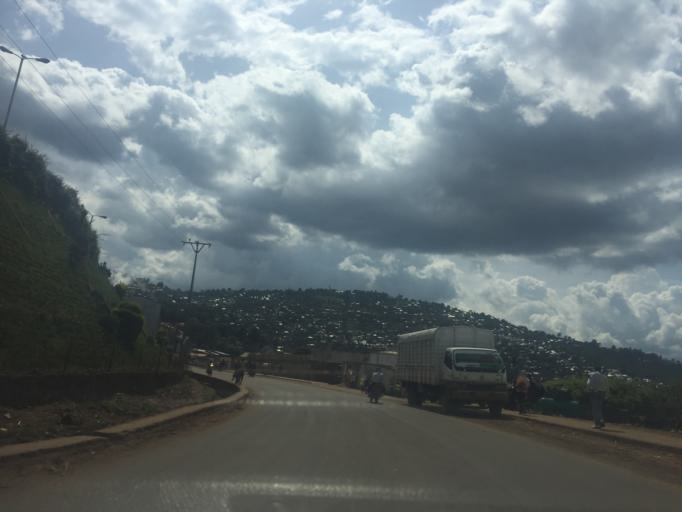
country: CD
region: South Kivu
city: Bukavu
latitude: -2.4840
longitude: 28.8451
